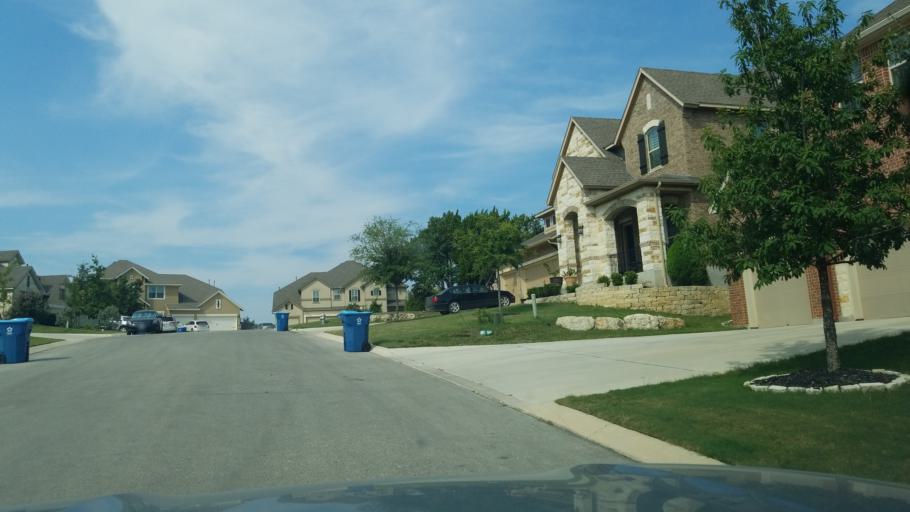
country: US
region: Texas
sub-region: Bexar County
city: Scenic Oaks
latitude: 29.7249
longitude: -98.6637
